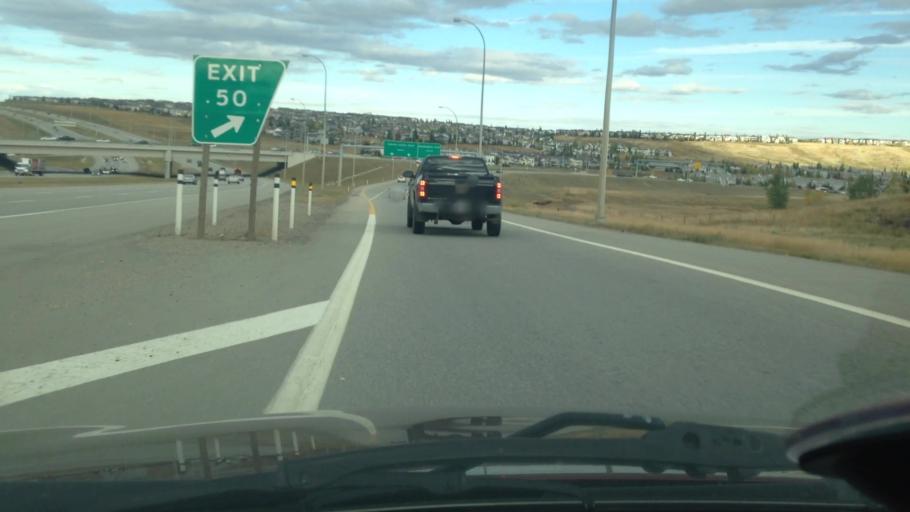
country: CA
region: Alberta
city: Calgary
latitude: 51.1547
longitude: -114.1199
